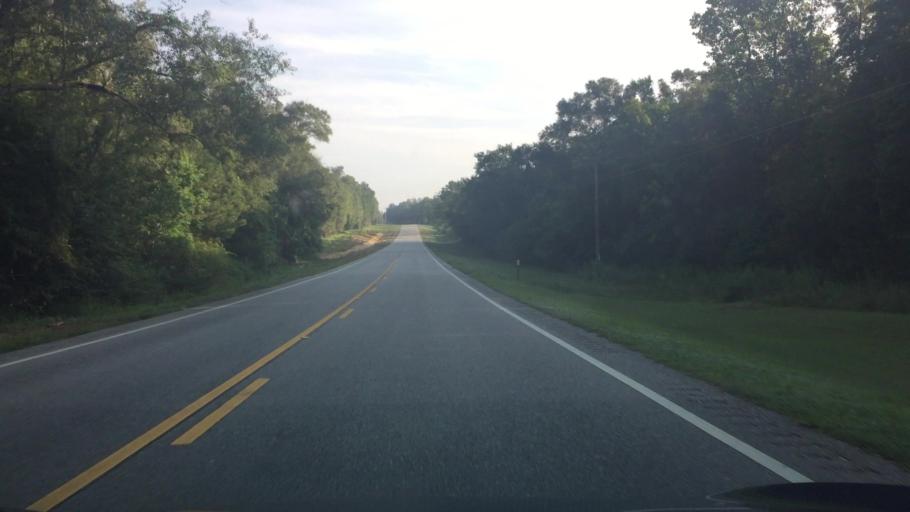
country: US
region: Alabama
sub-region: Covington County
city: Andalusia
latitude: 31.1545
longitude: -86.4584
